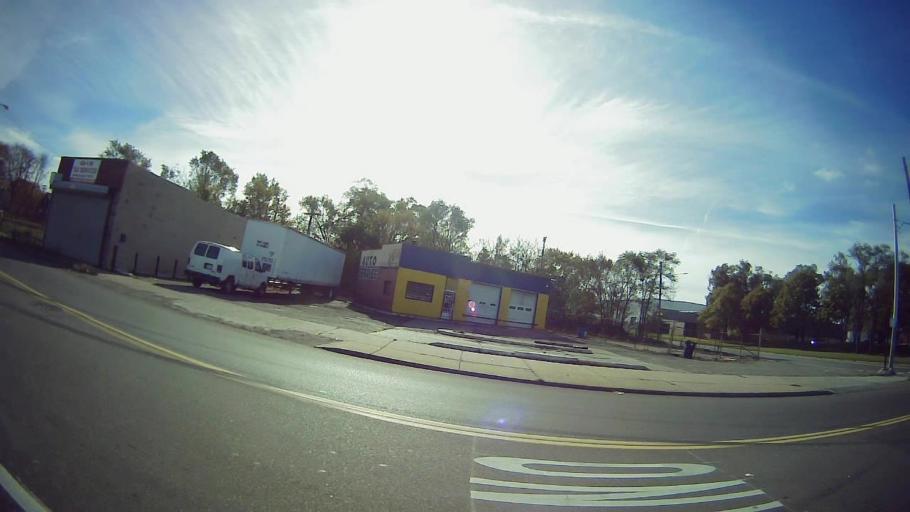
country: US
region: Michigan
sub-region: Wayne County
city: Hamtramck
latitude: 42.4338
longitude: -83.0336
